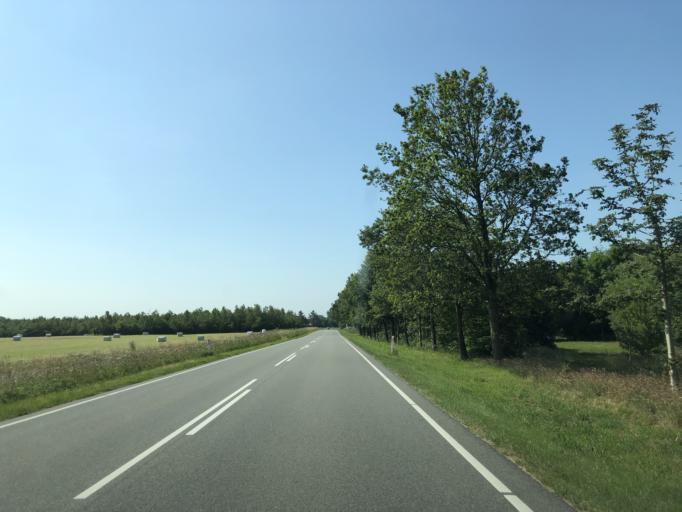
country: DK
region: South Denmark
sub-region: Varde Kommune
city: Varde
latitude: 55.6592
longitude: 8.4896
